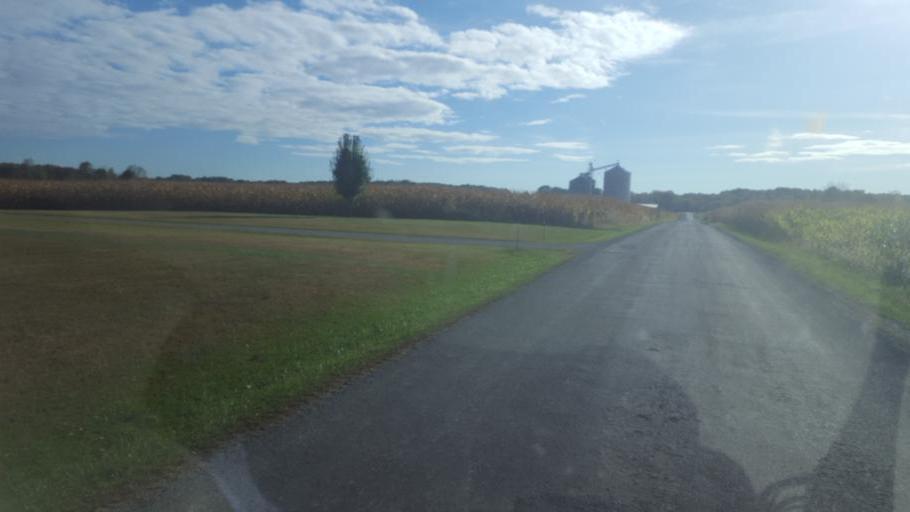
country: US
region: Pennsylvania
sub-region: Mercer County
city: Greenville
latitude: 41.3686
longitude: -80.2577
